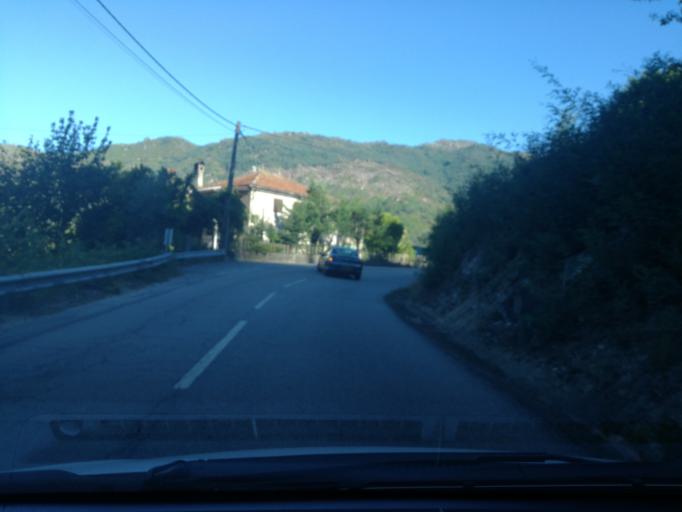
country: PT
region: Braga
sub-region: Vieira do Minho
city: Real
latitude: 41.6984
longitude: -8.1674
